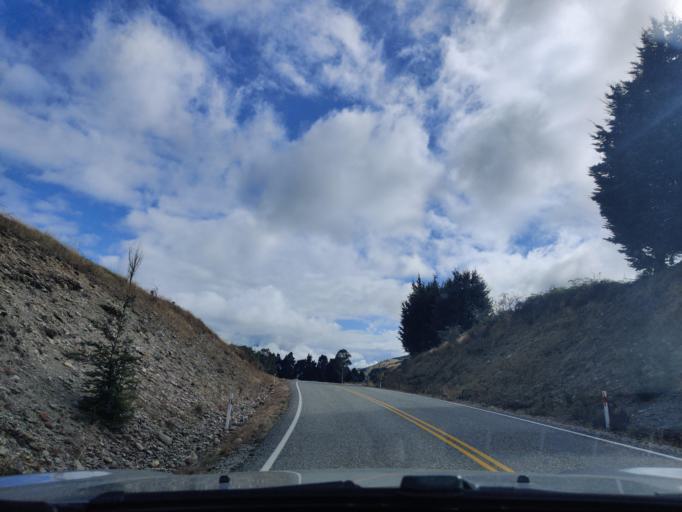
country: NZ
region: Otago
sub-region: Queenstown-Lakes District
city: Queenstown
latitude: -44.8691
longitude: 168.4034
